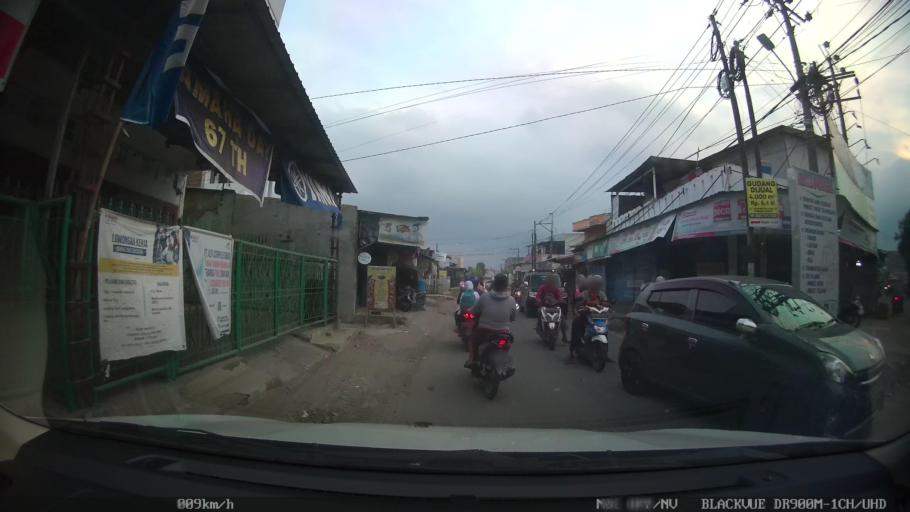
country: ID
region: North Sumatra
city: Sunggal
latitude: 3.5872
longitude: 98.6000
